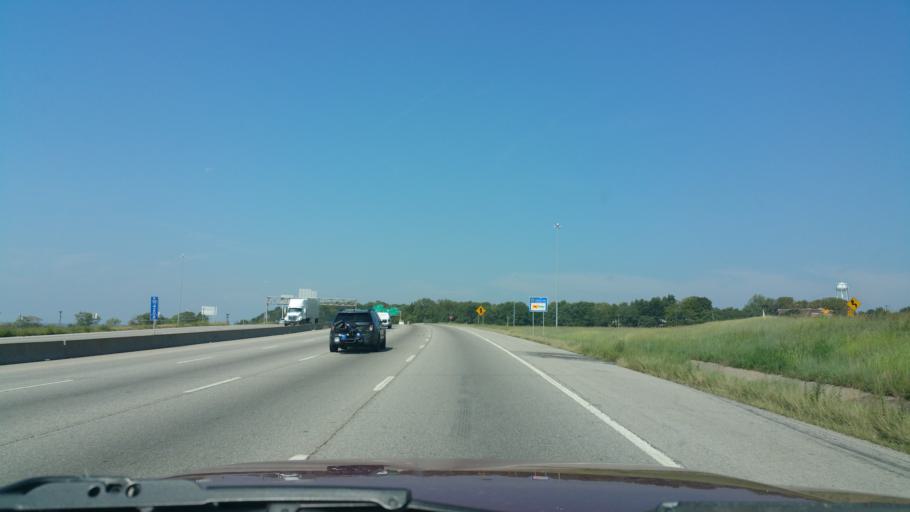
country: US
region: Kansas
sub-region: Wyandotte County
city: Kansas City
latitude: 39.0952
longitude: -94.6462
